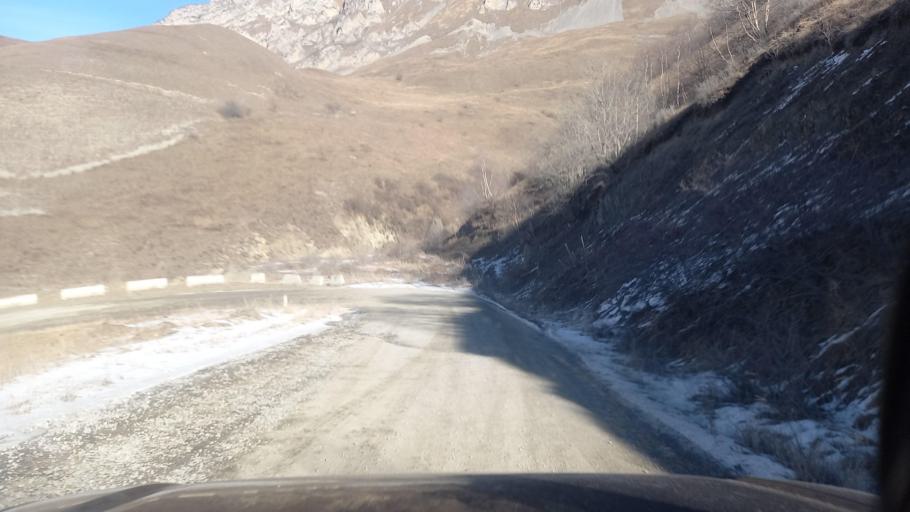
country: RU
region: North Ossetia
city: Verkhniy Fiagdon
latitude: 42.8394
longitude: 44.4648
